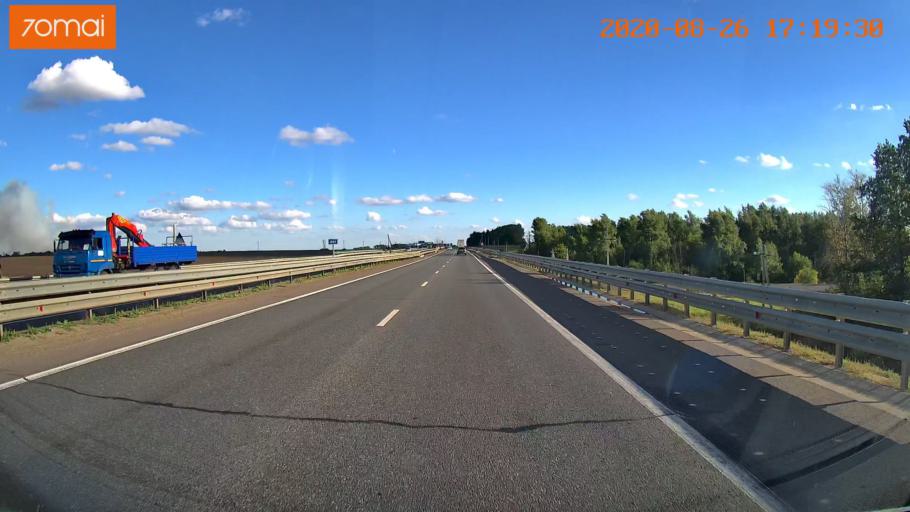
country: RU
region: Tula
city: Volovo
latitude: 53.5941
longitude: 38.1046
